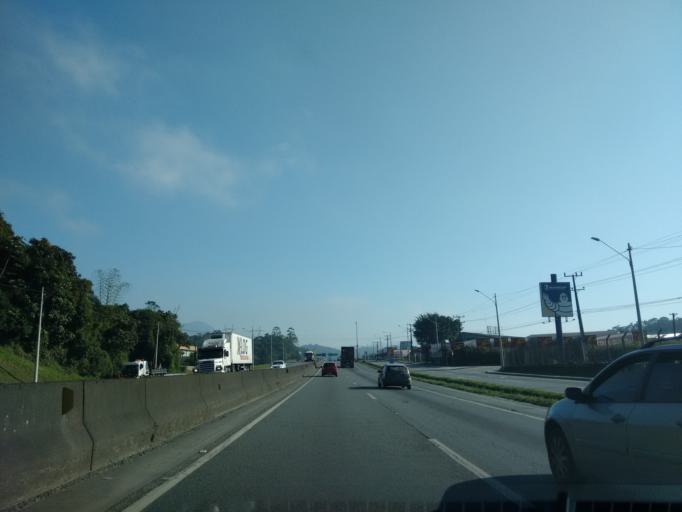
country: BR
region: Santa Catarina
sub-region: Joinville
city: Joinville
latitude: -26.2850
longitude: -48.8880
